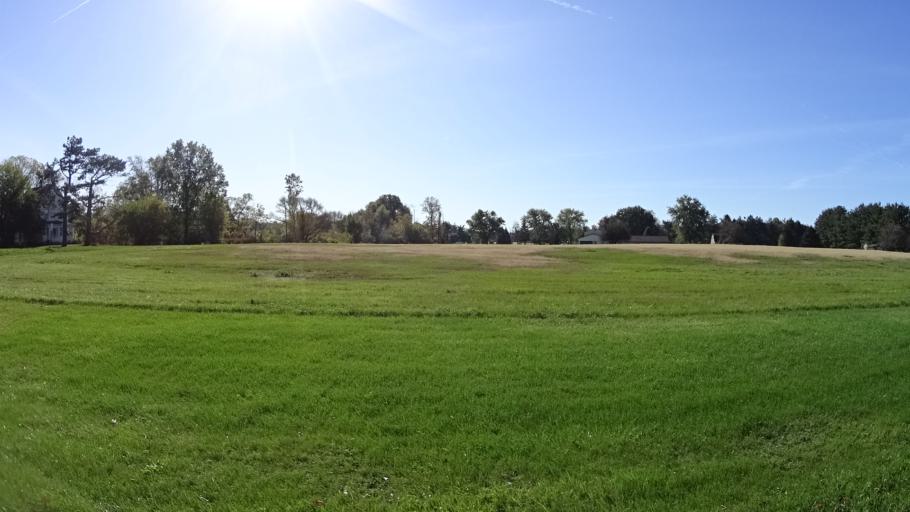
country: US
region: Ohio
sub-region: Lorain County
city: Vermilion-on-the-Lake
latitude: 41.3990
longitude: -82.2836
